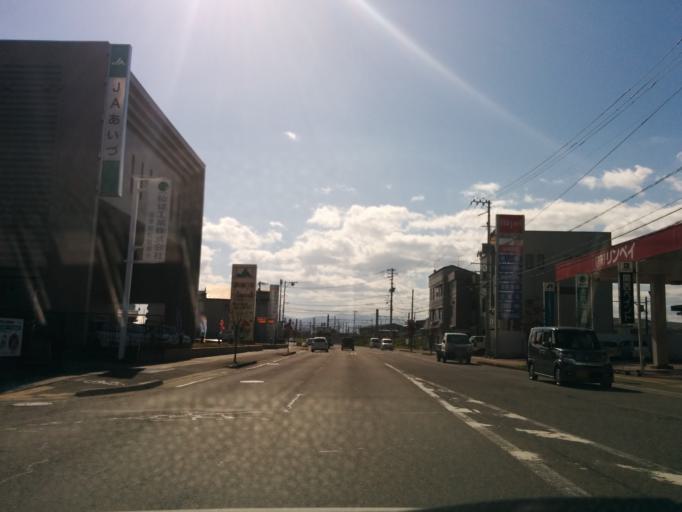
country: JP
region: Fukushima
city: Kitakata
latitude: 37.5151
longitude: 139.9323
